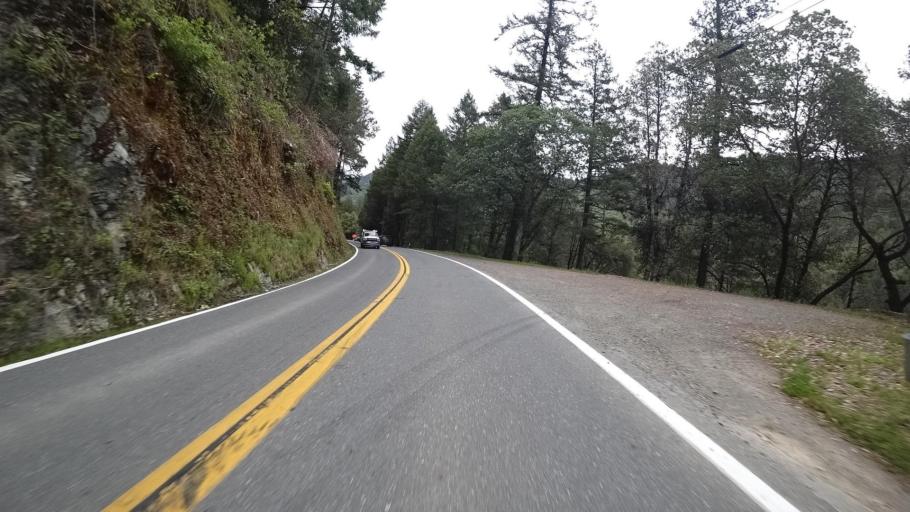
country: US
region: California
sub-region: Humboldt County
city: Willow Creek
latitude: 41.0182
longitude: -123.6373
